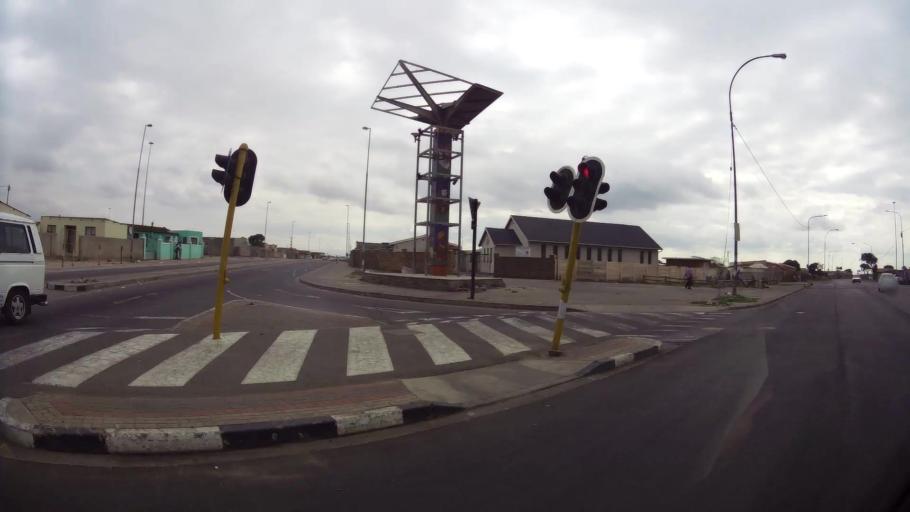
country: ZA
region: Eastern Cape
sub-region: Nelson Mandela Bay Metropolitan Municipality
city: Port Elizabeth
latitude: -33.8940
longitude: 25.5920
